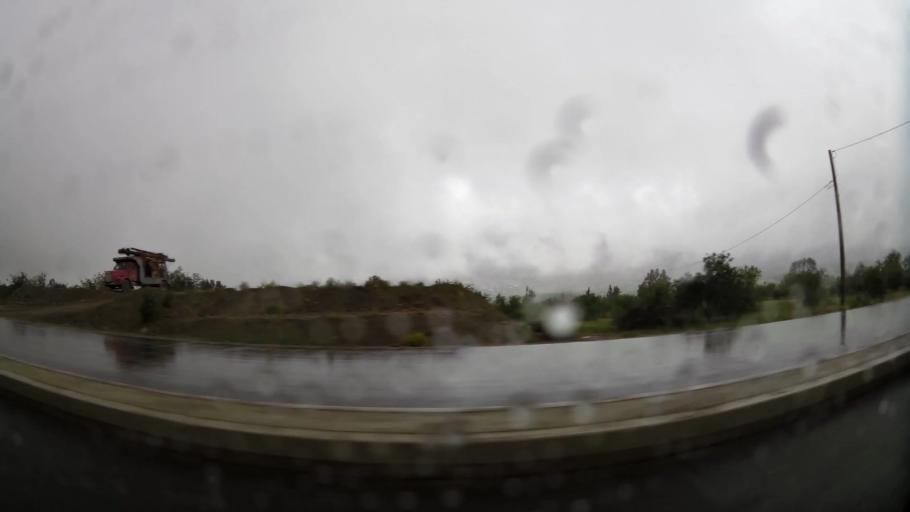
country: MA
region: Oriental
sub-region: Nador
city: Midar
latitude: 34.8453
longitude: -3.7214
